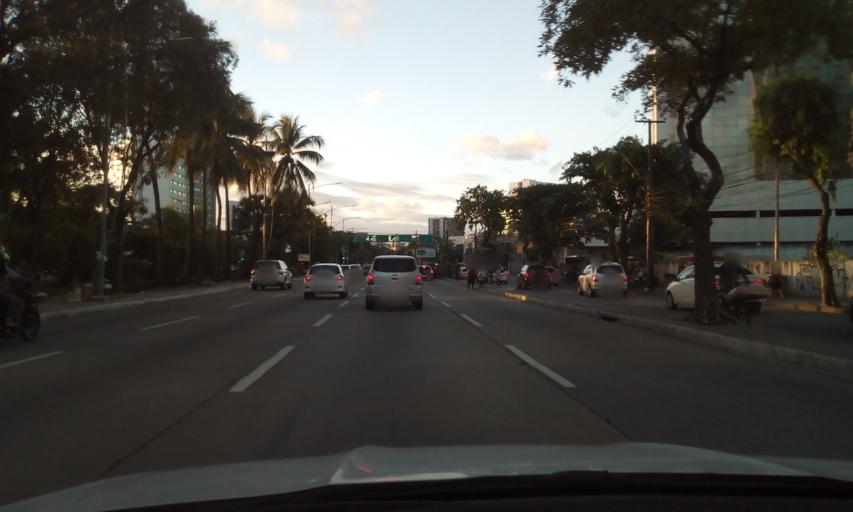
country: BR
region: Pernambuco
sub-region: Recife
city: Recife
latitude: -8.0637
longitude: -34.8972
